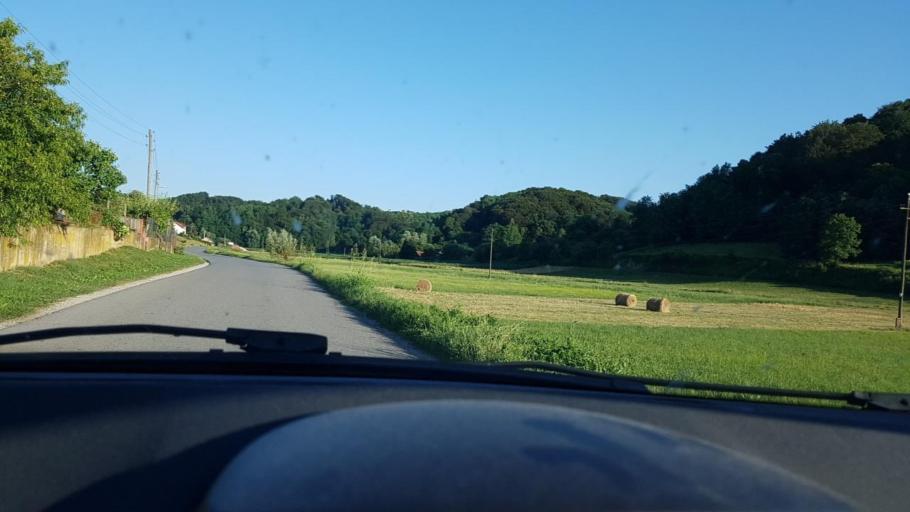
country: HR
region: Krapinsko-Zagorska
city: Mihovljan
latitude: 46.0890
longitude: 15.9628
